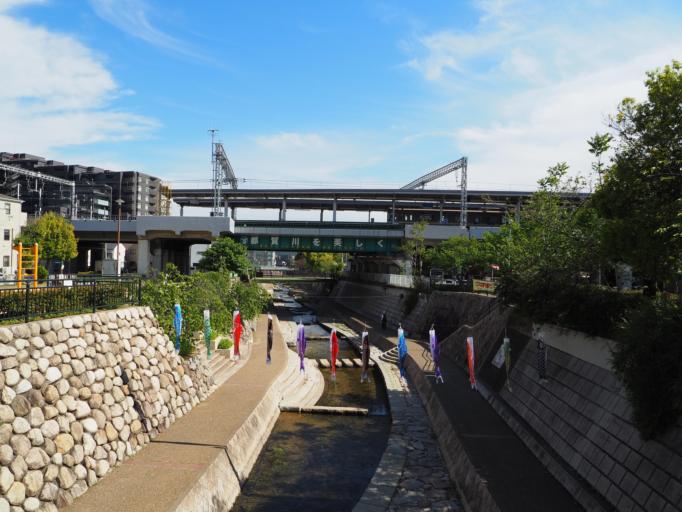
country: JP
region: Hyogo
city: Kobe
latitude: 34.7084
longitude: 135.2311
